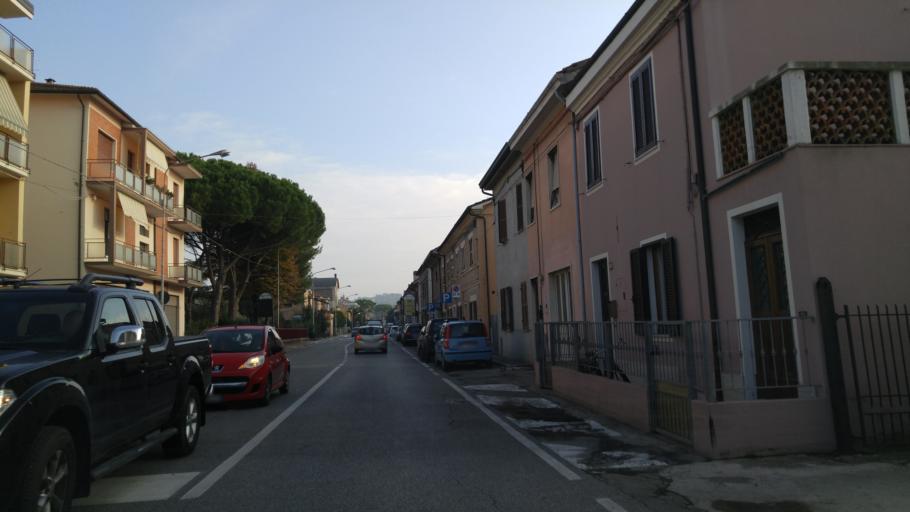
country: IT
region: The Marches
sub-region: Provincia di Pesaro e Urbino
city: Pesaro
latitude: 43.8971
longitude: 12.9211
